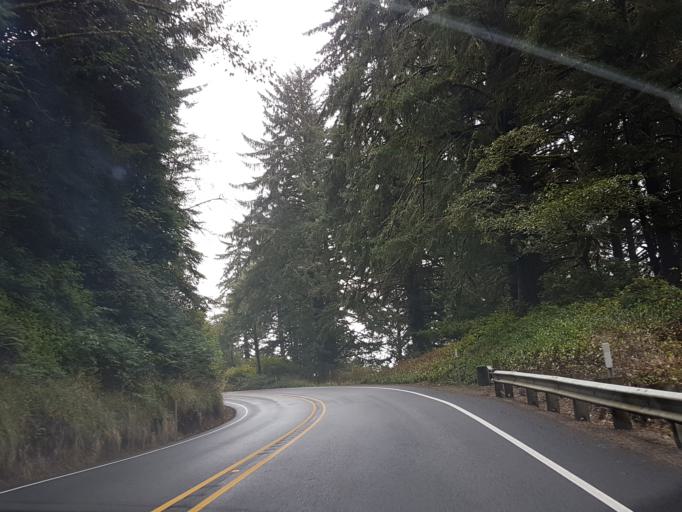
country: US
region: Oregon
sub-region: Lane County
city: Florence
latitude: 44.1170
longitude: -124.1196
